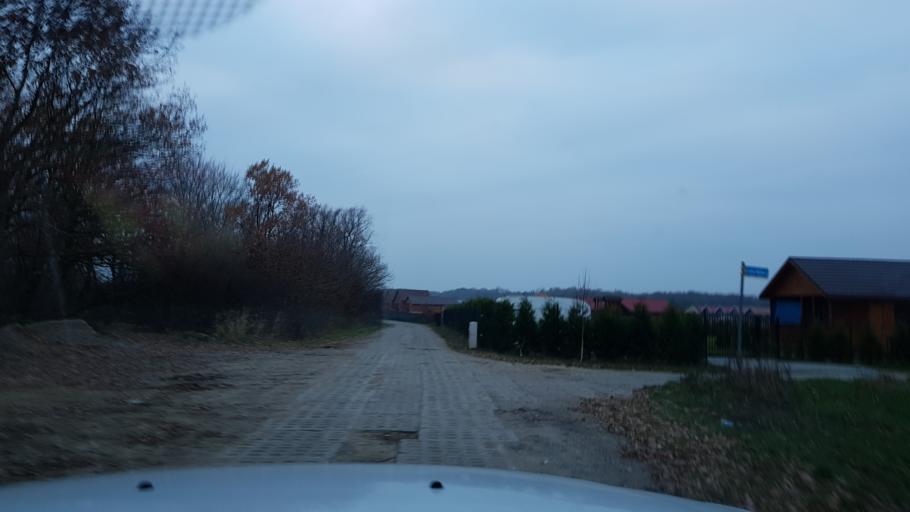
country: PL
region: West Pomeranian Voivodeship
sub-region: Powiat slawienski
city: Darlowo
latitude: 54.5109
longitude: 16.4960
